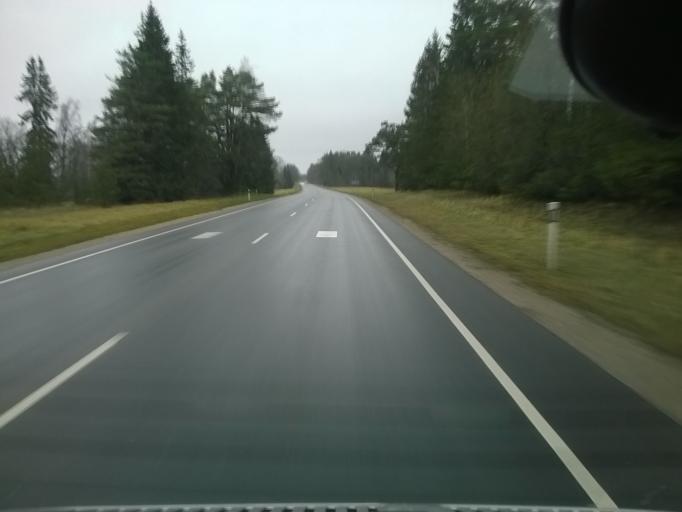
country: EE
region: Harju
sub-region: Nissi vald
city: Turba
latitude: 59.0101
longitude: 24.1315
